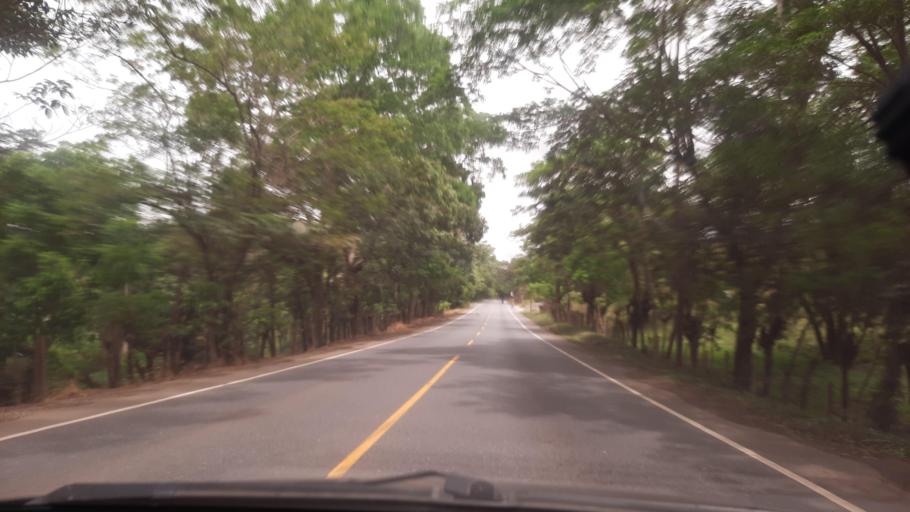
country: GT
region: Izabal
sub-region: Municipio de Los Amates
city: Los Amates
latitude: 15.2322
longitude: -89.1940
